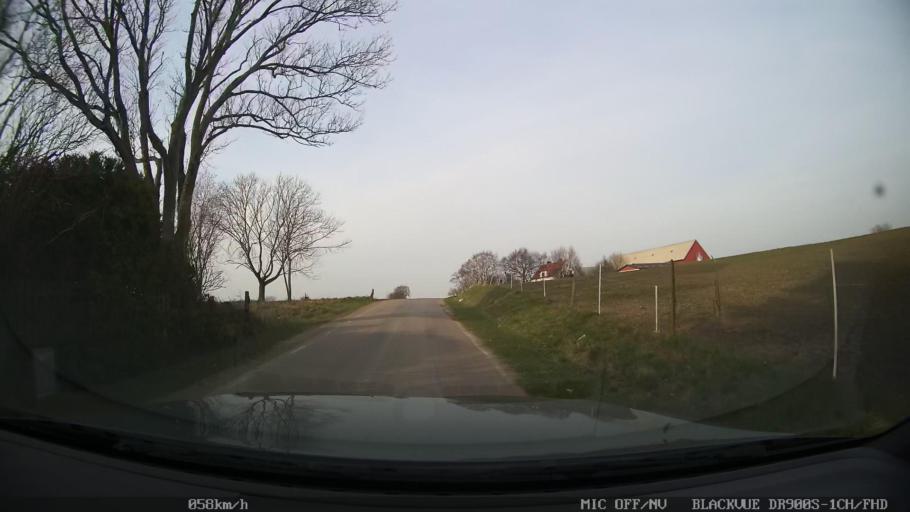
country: SE
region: Skane
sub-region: Ystads Kommun
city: Ystad
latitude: 55.4718
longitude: 13.8003
